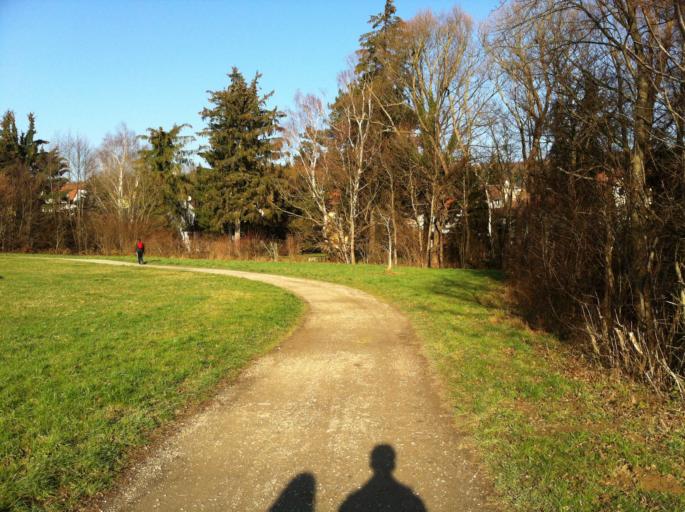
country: AT
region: Lower Austria
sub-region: Politischer Bezirk Wien-Umgebung
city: Gablitz
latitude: 48.2310
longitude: 16.1465
